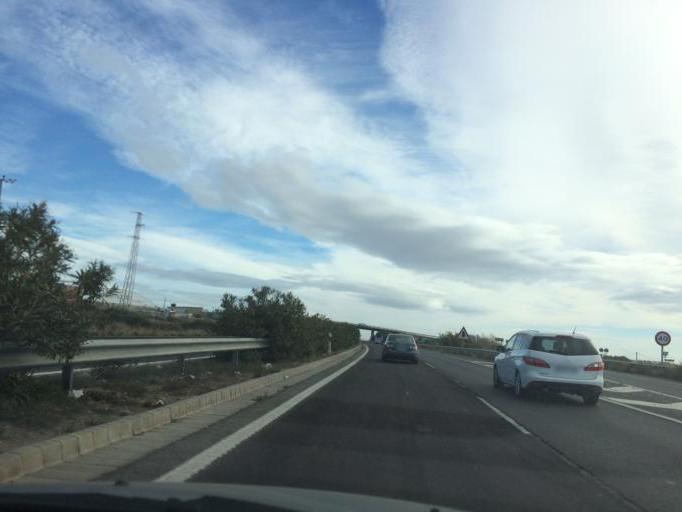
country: ES
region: Andalusia
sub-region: Provincia de Almeria
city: Viator
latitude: 36.8436
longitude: -2.4021
